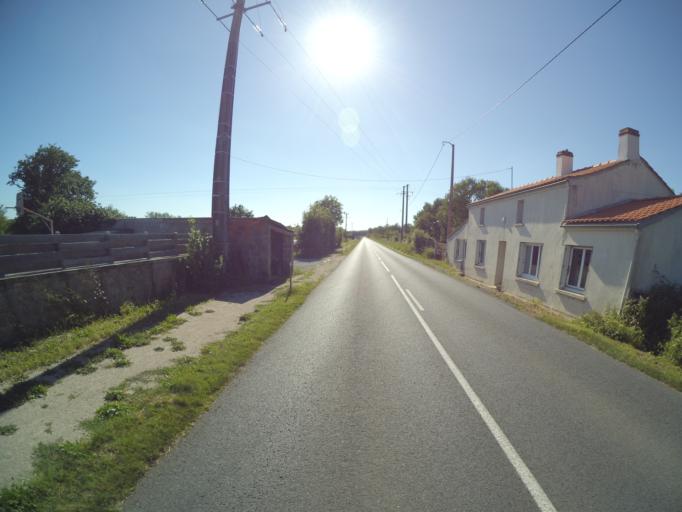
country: FR
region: Pays de la Loire
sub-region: Departement de la Vendee
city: La Guyonniere
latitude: 46.9578
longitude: -1.2373
